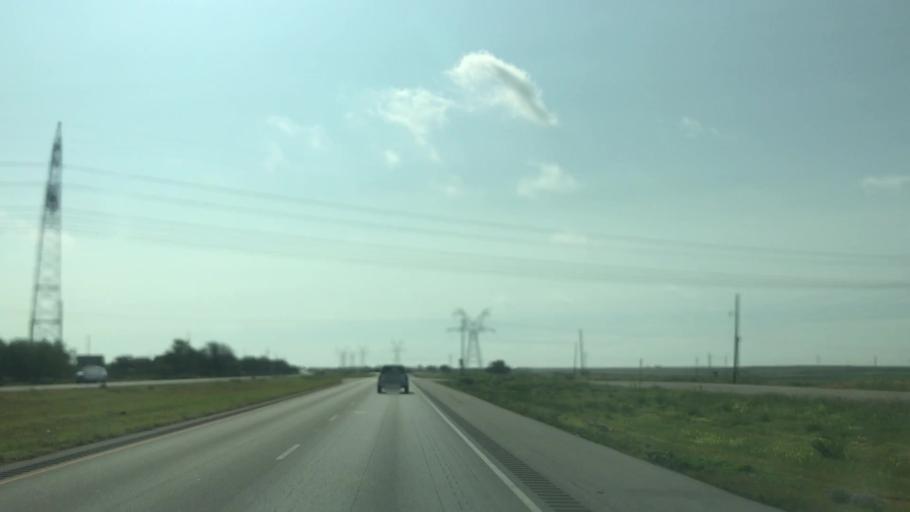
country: US
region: Texas
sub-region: Scurry County
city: Snyder
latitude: 32.6835
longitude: -100.8353
